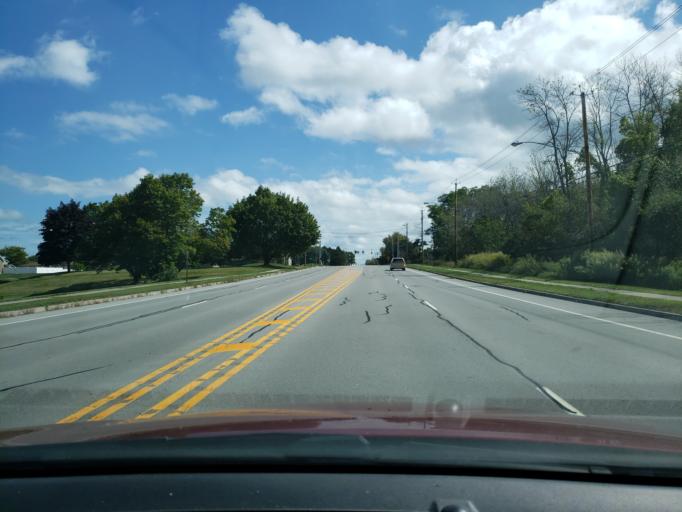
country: US
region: New York
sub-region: Monroe County
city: Greece
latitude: 43.2532
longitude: -77.7093
